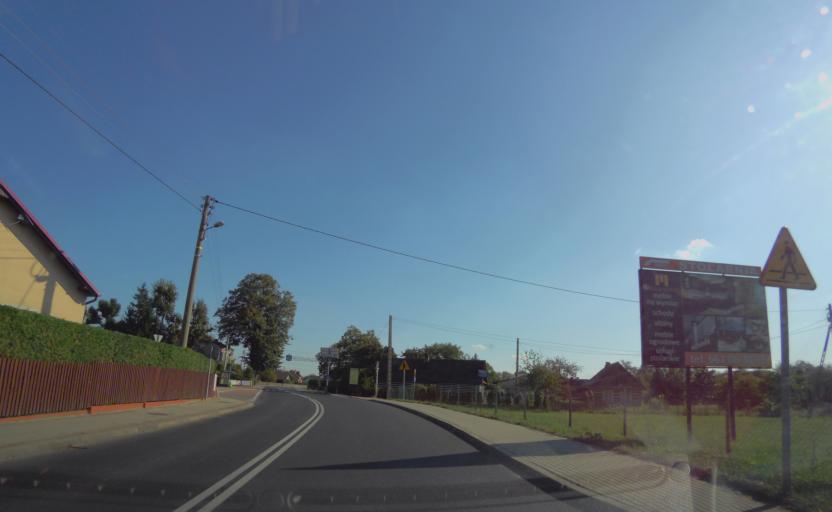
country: PL
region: Subcarpathian Voivodeship
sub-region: Powiat lezajski
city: Stare Miasto
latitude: 50.2868
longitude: 22.4286
